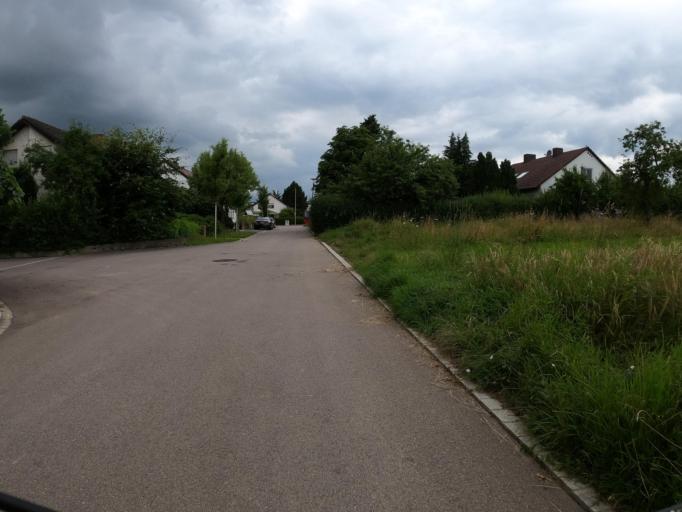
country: DE
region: Baden-Wuerttemberg
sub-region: Tuebingen Region
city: Langenau
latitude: 48.5029
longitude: 10.1197
